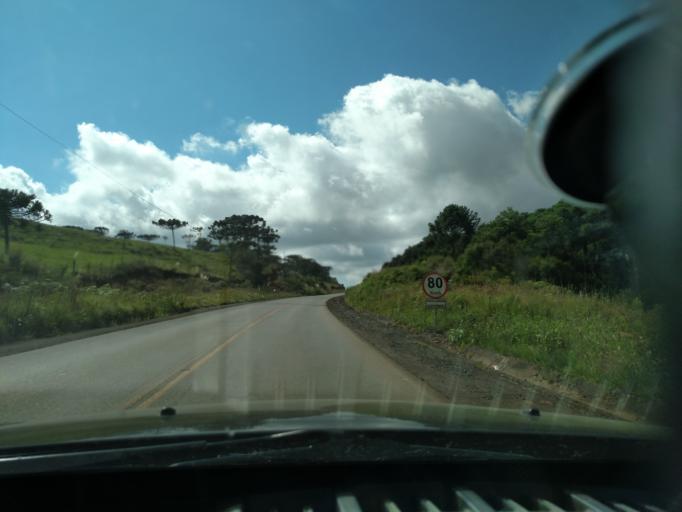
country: BR
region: Santa Catarina
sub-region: Lages
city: Lages
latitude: -27.8950
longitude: -50.1305
